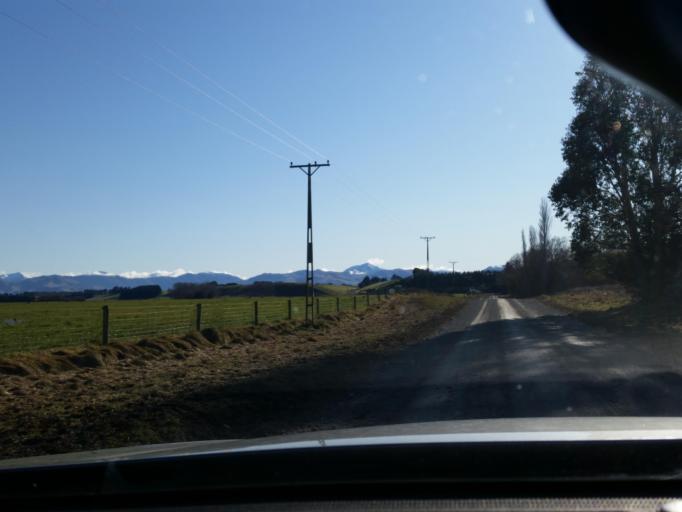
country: NZ
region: Southland
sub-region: Gore District
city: Gore
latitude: -45.8390
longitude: 168.7389
